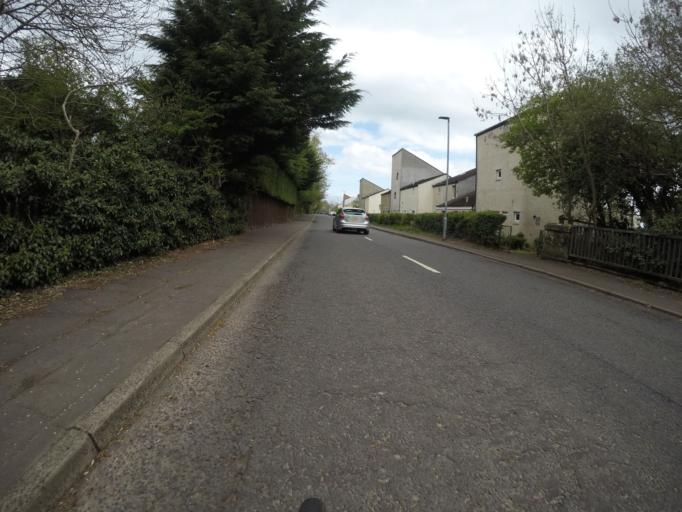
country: GB
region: Scotland
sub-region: North Ayrshire
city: Irvine
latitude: 55.6282
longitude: -4.6311
